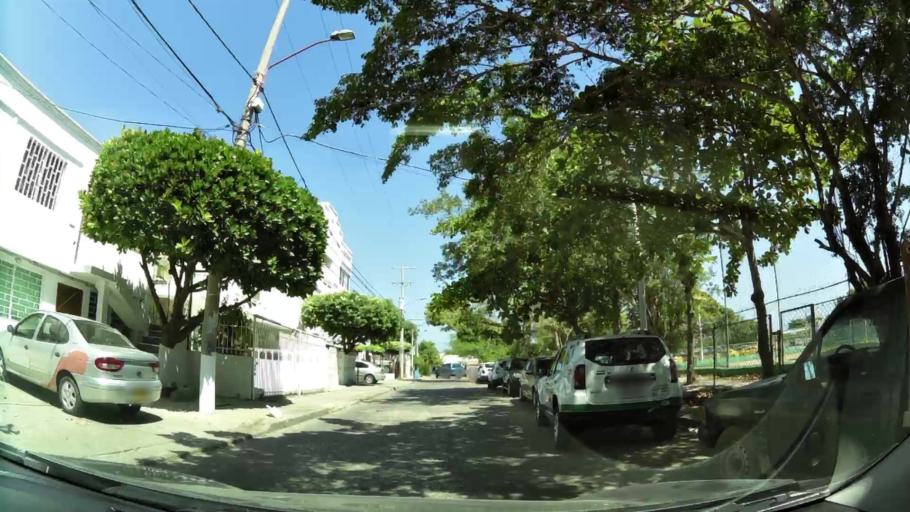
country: CO
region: Bolivar
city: Cartagena
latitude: 10.4436
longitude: -75.5159
